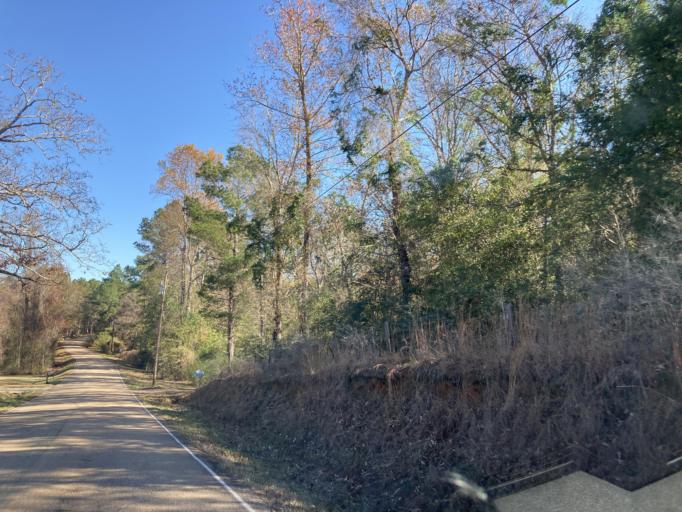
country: US
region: Mississippi
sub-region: Lamar County
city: Sumrall
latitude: 31.2726
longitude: -89.5245
